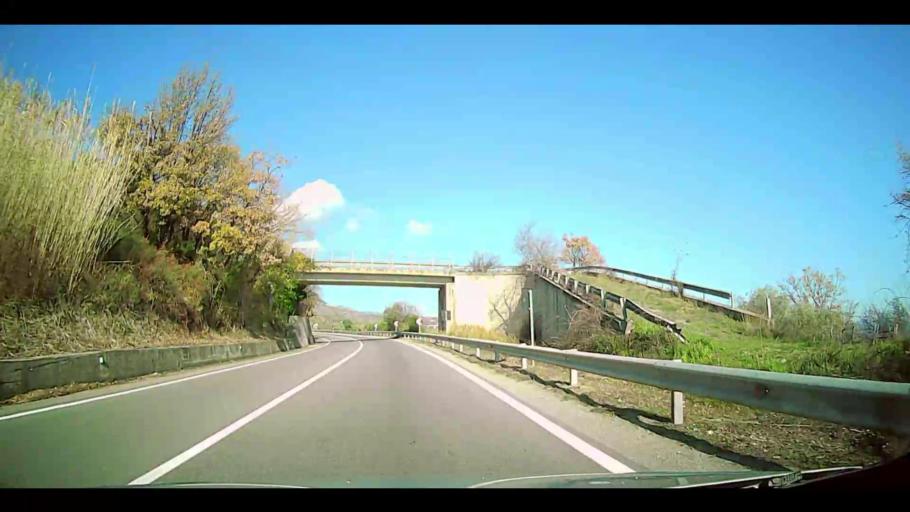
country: IT
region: Calabria
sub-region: Provincia di Crotone
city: Caccuri
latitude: 39.2067
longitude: 16.8050
